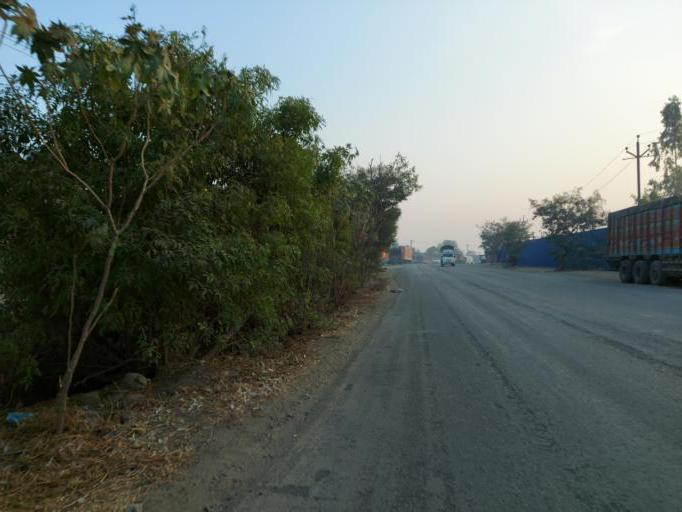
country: IN
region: Maharashtra
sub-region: Pune Division
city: Pune
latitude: 18.4658
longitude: 73.9544
